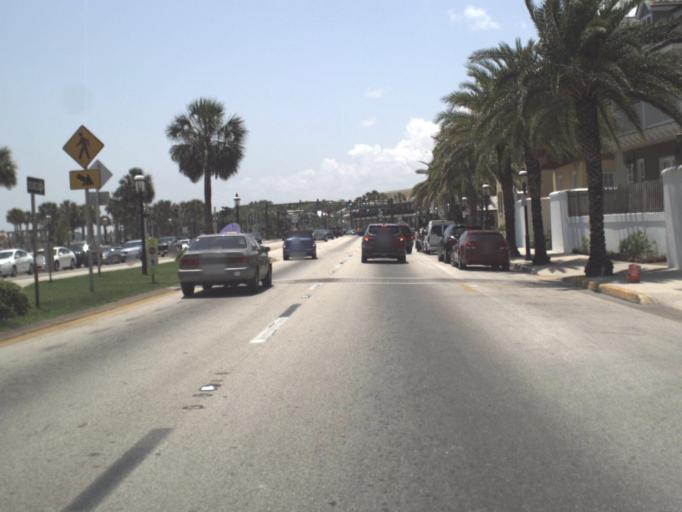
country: US
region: Florida
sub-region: Saint Johns County
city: Saint Augustine
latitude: 29.8945
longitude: -81.3111
